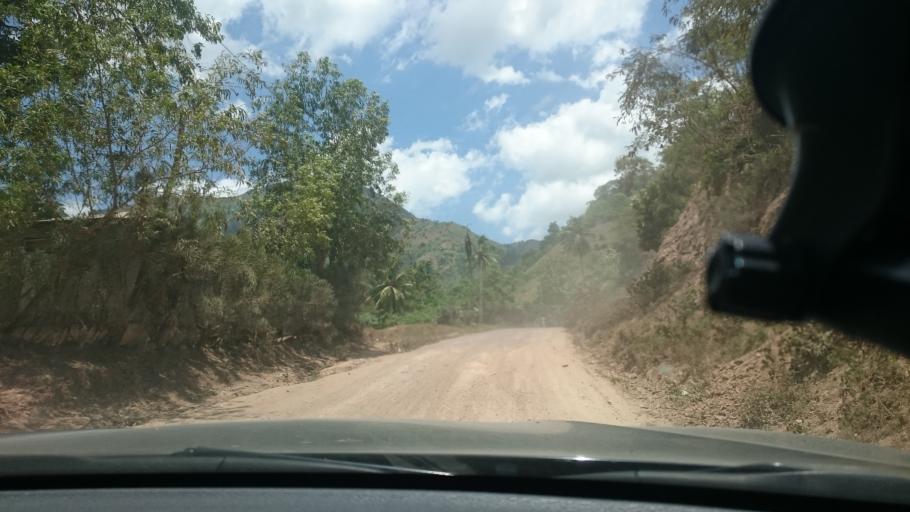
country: HT
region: Nord
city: Milot
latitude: 19.5930
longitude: -72.1930
